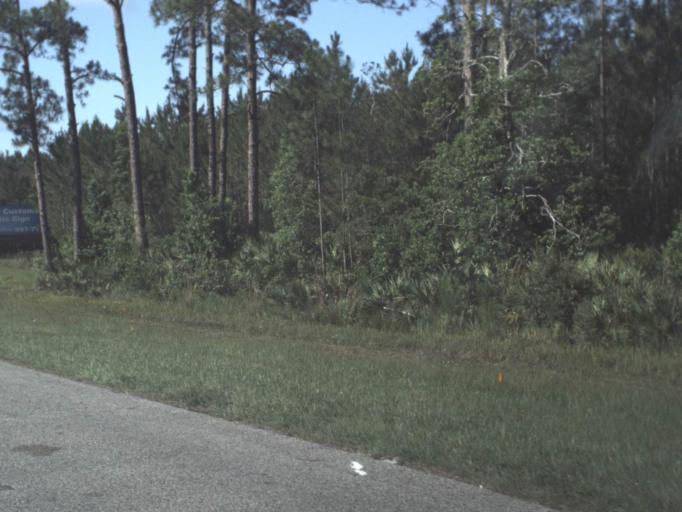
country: US
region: Florida
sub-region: Saint Johns County
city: Saint Augustine Shores
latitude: 29.7872
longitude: -81.3624
